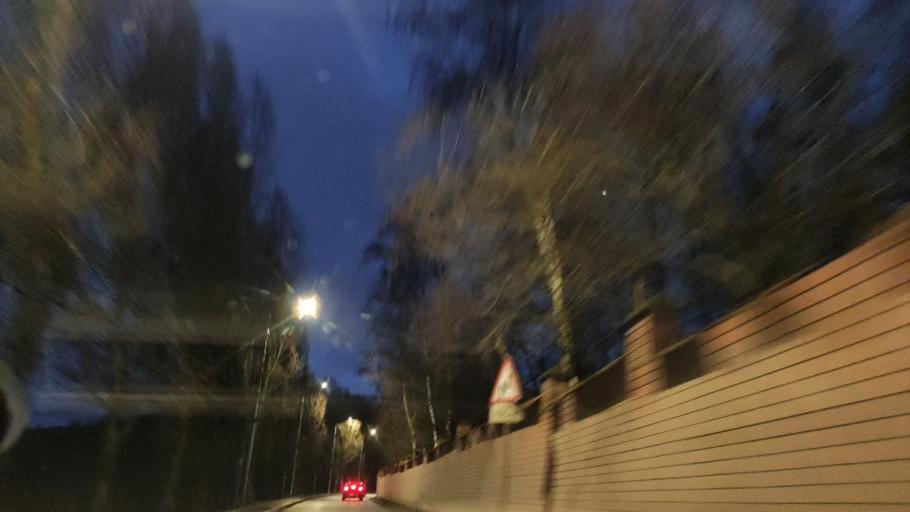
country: RU
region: Moskovskaya
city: Biryulevo Zapadnoye
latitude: 55.5569
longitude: 37.6337
